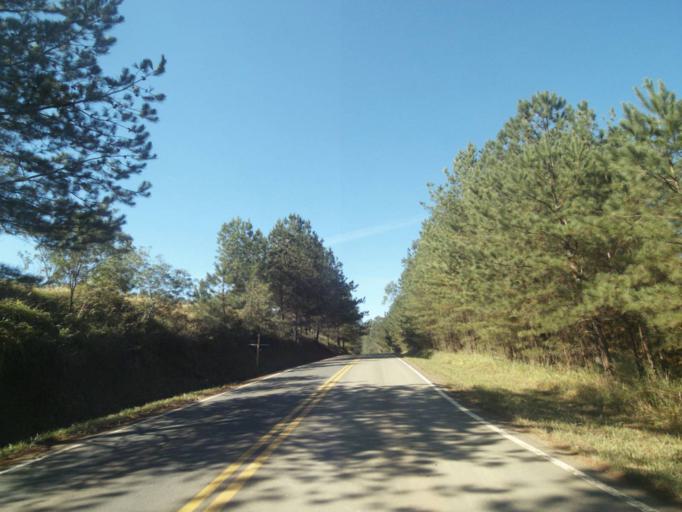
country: BR
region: Parana
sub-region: Telemaco Borba
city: Telemaco Borba
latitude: -24.4161
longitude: -50.5912
